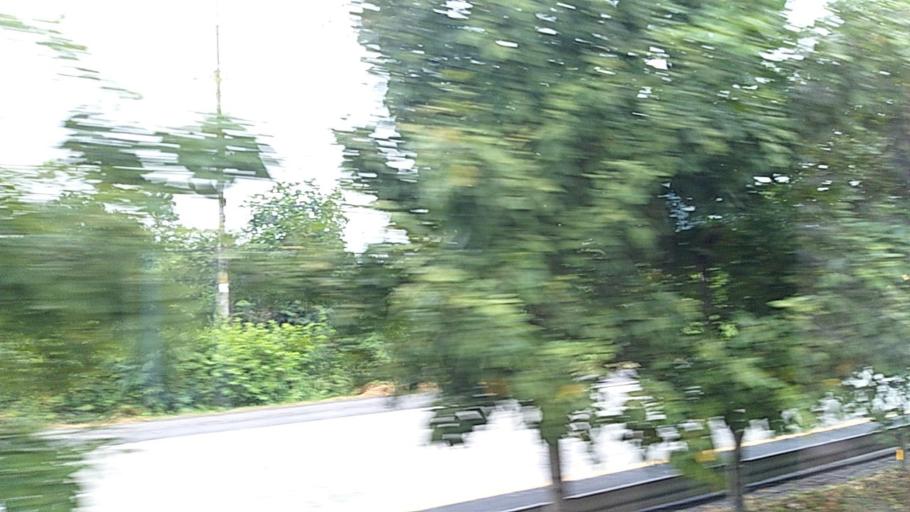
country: TH
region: Nakhon Ratchasima
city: Phimai
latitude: 15.2802
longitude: 102.4184
